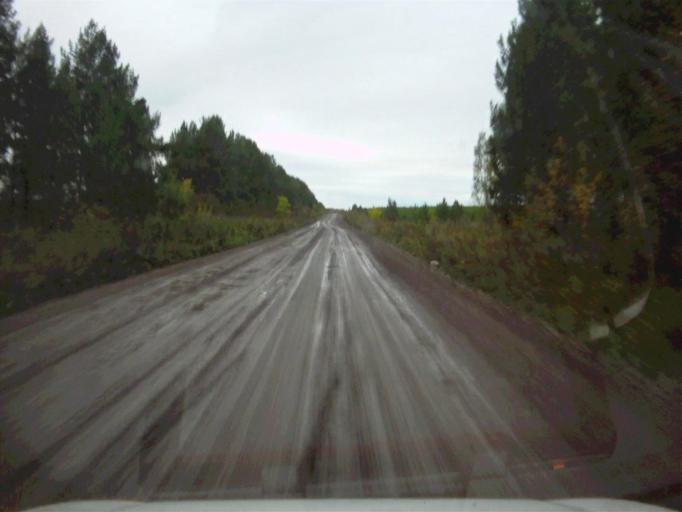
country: RU
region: Chelyabinsk
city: Nyazepetrovsk
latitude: 56.1439
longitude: 59.2859
